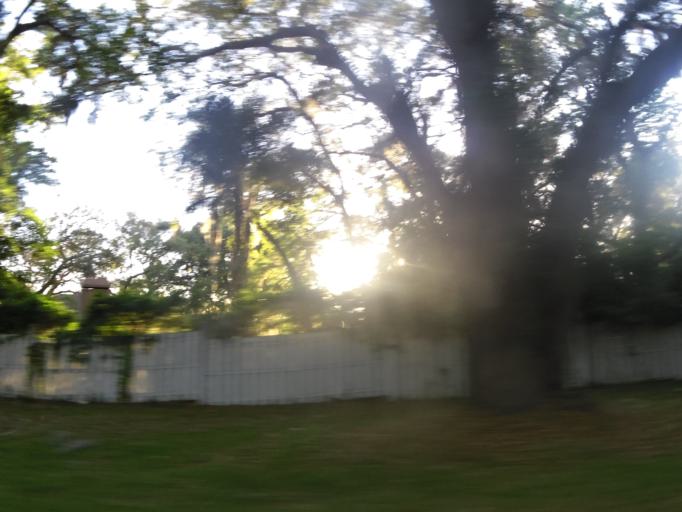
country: US
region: Florida
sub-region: Duval County
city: Atlantic Beach
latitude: 30.3625
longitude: -81.5156
